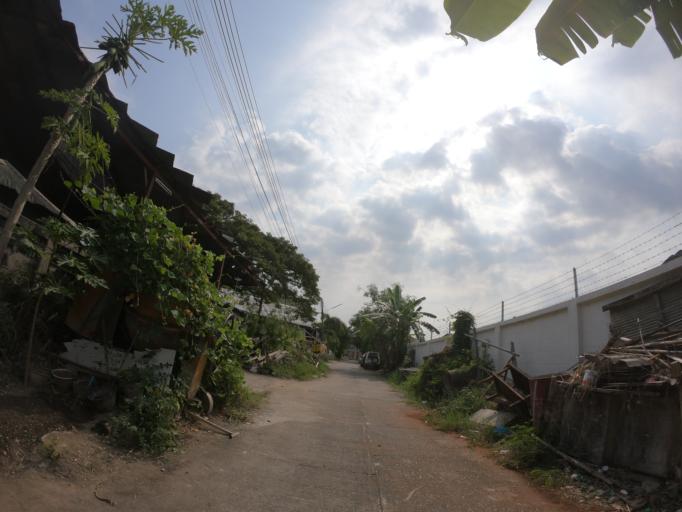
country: TH
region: Chiang Mai
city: Chiang Mai
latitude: 18.7575
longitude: 98.9670
